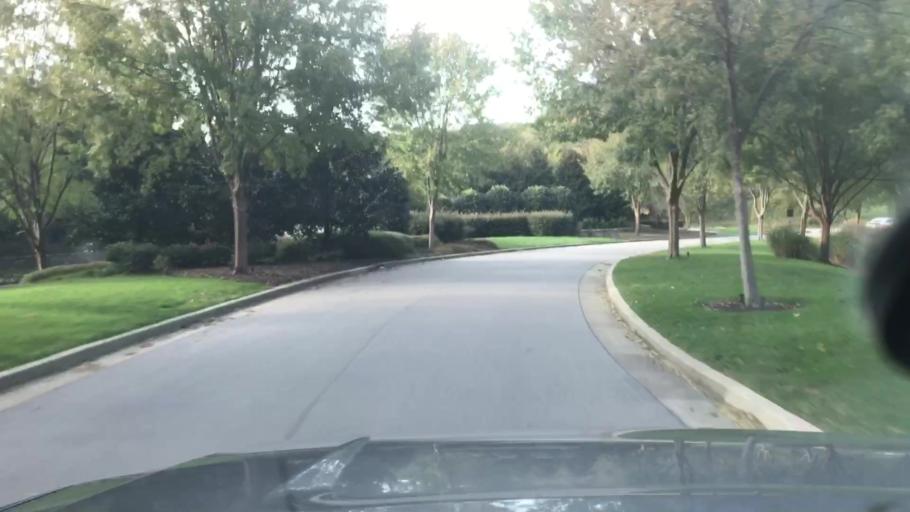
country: US
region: Tennessee
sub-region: Williamson County
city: Brentwood
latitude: 36.0118
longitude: -86.8326
